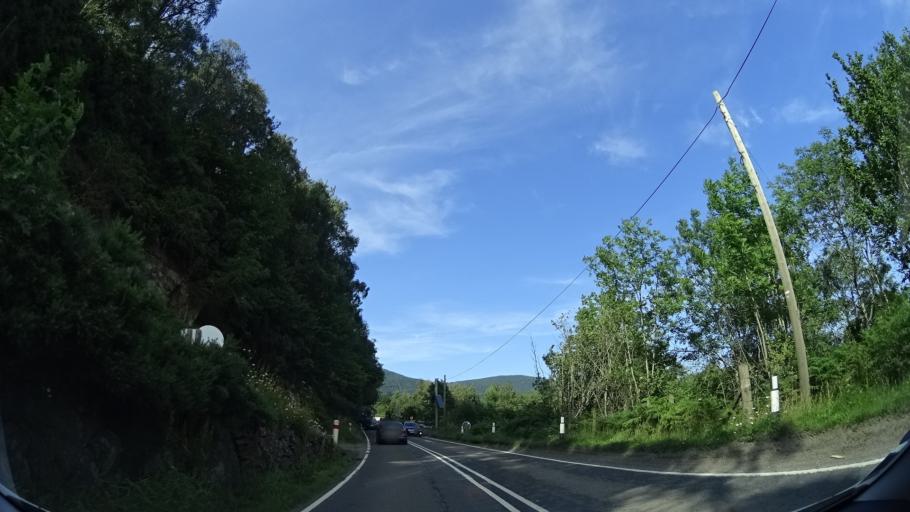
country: GB
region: Scotland
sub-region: Highland
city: Beauly
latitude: 57.3228
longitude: -4.4451
